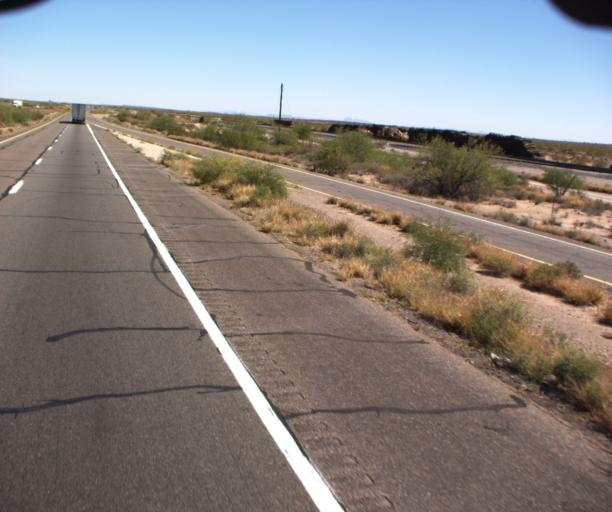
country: US
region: Arizona
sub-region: Maricopa County
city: Gila Bend
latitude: 32.8586
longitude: -113.2096
